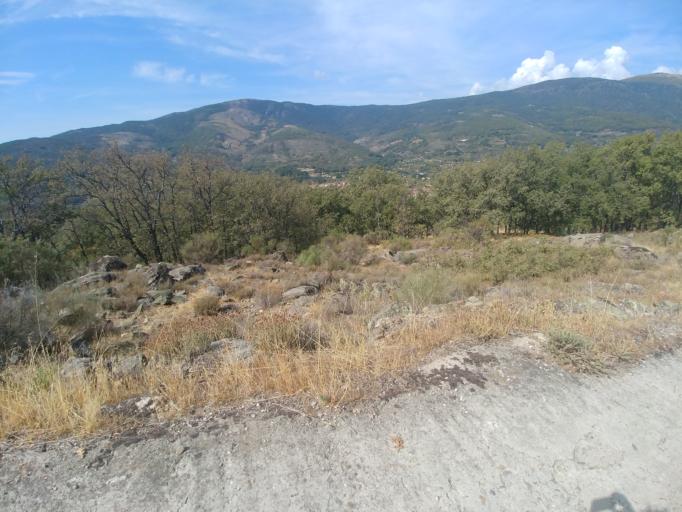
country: ES
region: Extremadura
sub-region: Provincia de Caceres
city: Garganta la Olla
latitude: 40.1061
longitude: -5.7639
